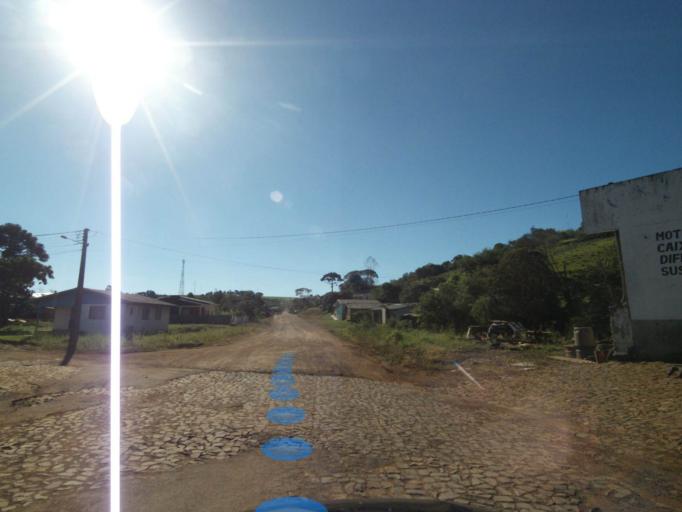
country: BR
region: Parana
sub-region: Coronel Vivida
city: Coronel Vivida
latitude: -26.1424
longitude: -52.3825
